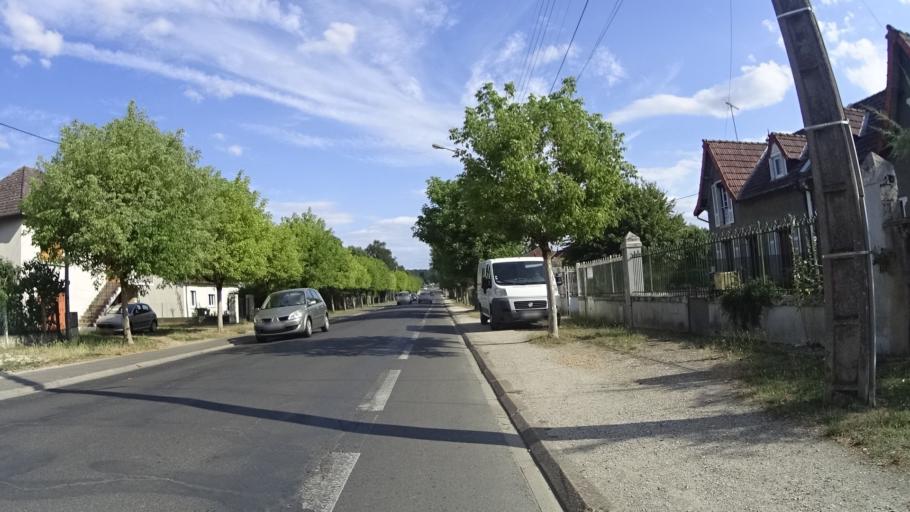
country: FR
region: Centre
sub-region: Departement du Loir-et-Cher
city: Chaumont-sur-Loire
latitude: 47.4895
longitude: 1.1872
